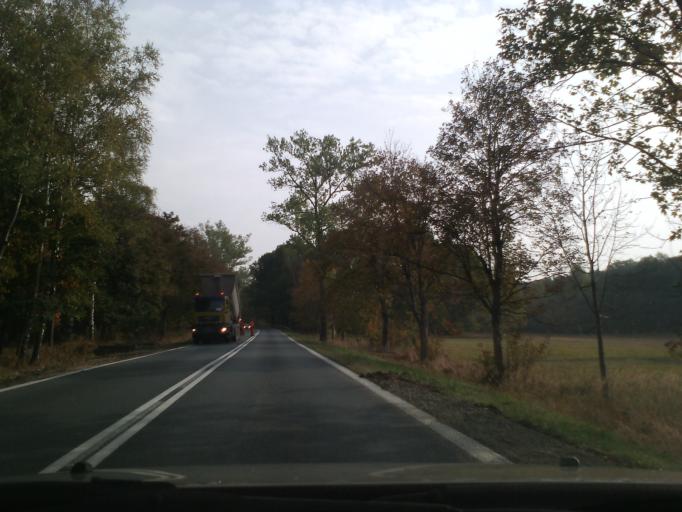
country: PL
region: Lower Silesian Voivodeship
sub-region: Powiat jeleniogorski
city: Janowice Wielkie
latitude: 50.9014
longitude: 15.8701
